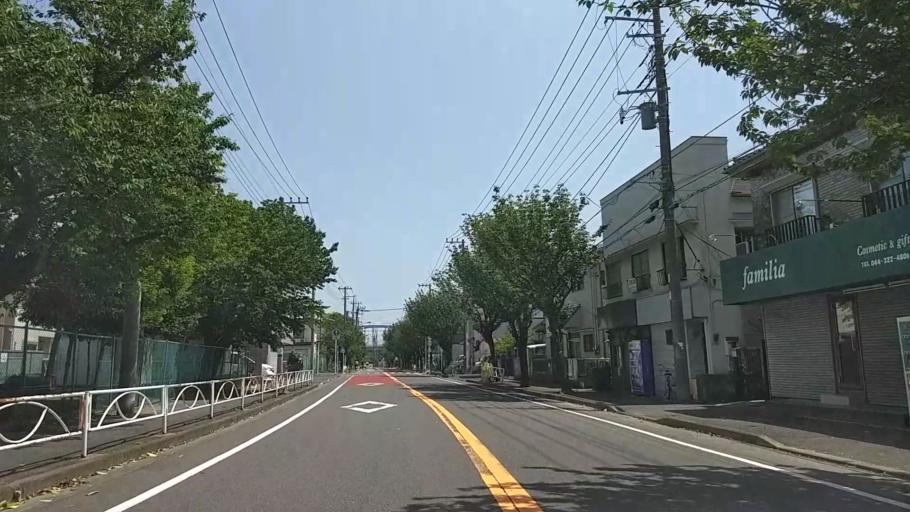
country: JP
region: Kanagawa
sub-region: Kawasaki-shi
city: Kawasaki
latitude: 35.5185
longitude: 139.7201
